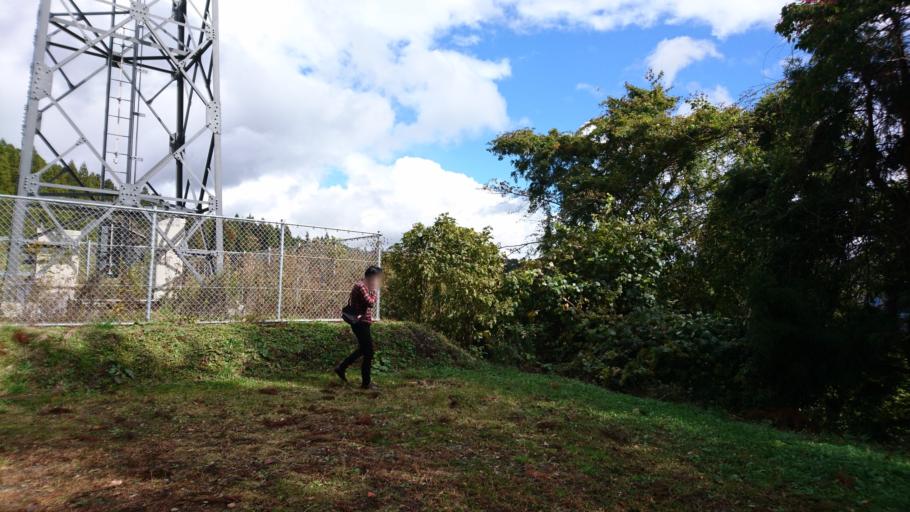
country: JP
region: Iwate
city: Ichinoseki
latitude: 38.9811
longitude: 141.1631
